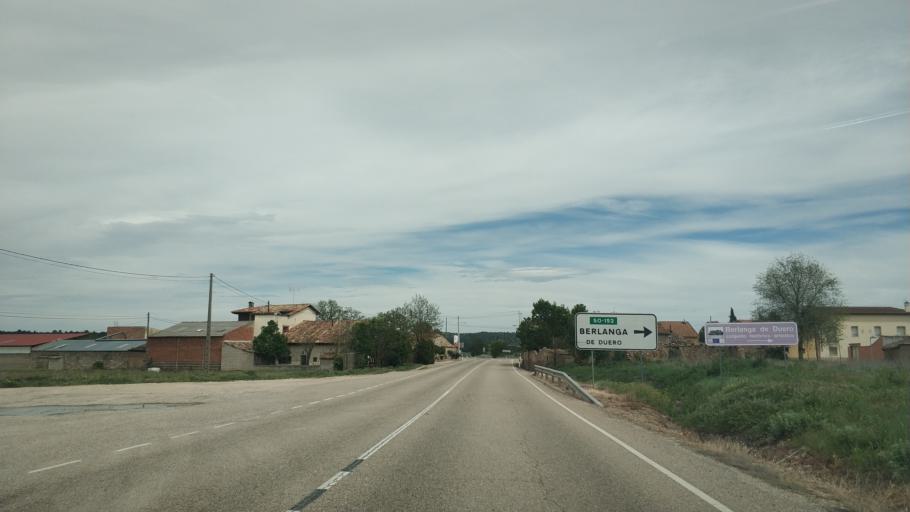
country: ES
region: Castille and Leon
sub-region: Provincia de Soria
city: Berlanga de Duero
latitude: 41.4957
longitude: -2.8707
